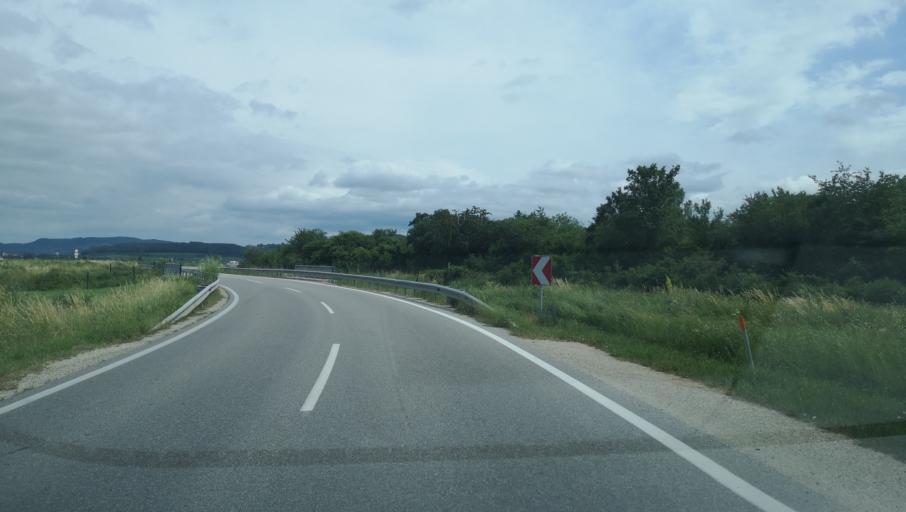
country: AT
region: Lower Austria
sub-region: Politischer Bezirk Krems
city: Weinzierl bei Krems
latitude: 48.3937
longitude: 15.5962
